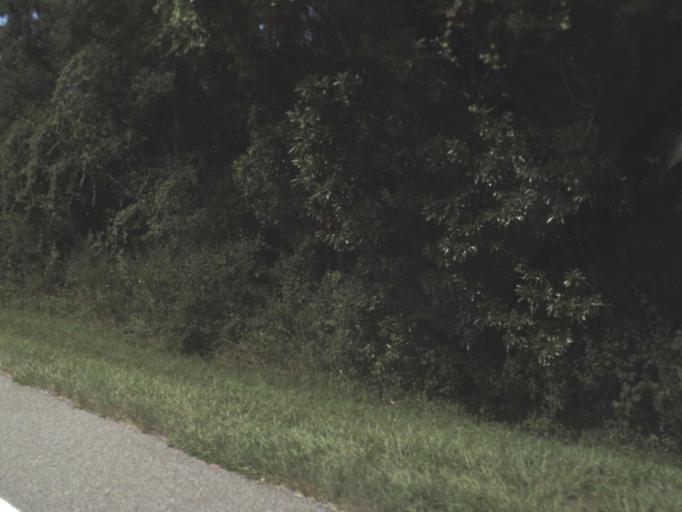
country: US
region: Florida
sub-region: Sarasota County
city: Lake Sarasota
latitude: 27.3667
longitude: -82.2093
